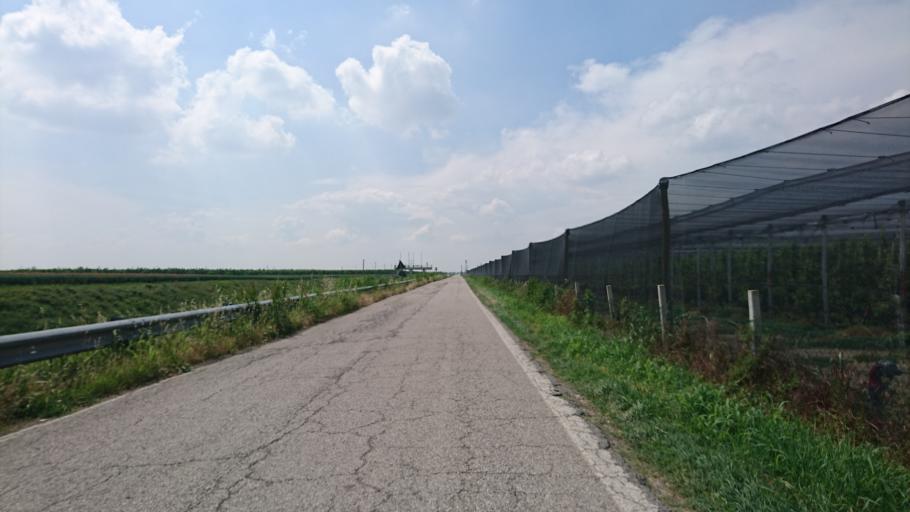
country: IT
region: Veneto
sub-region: Provincia di Rovigo
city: Giacciano con Baruchella
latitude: 45.0701
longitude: 11.4241
